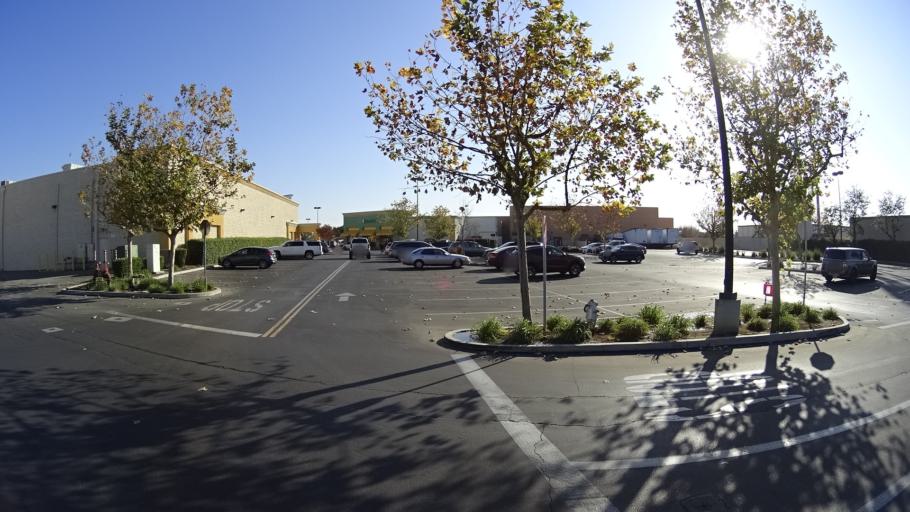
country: US
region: California
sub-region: Kern County
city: Greenacres
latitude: 35.3862
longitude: -119.1070
